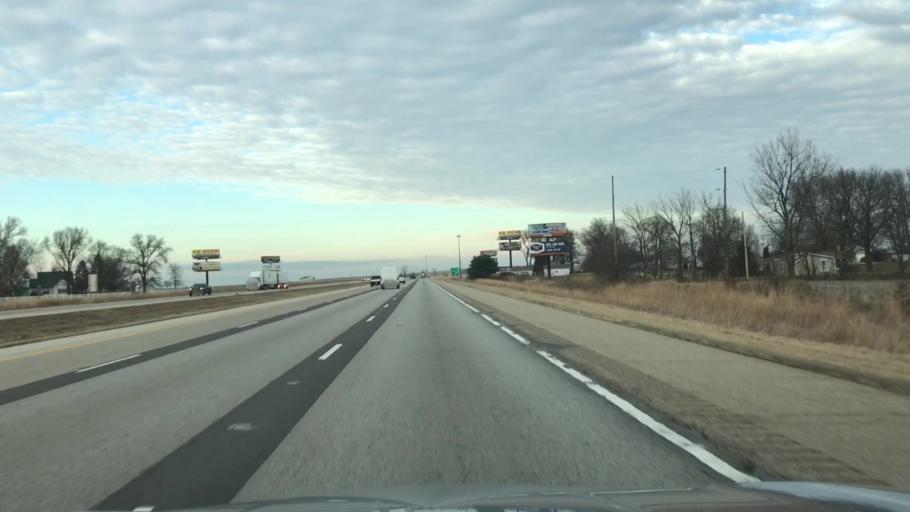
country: US
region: Illinois
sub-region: Logan County
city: Lincoln
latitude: 40.0660
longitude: -89.4475
